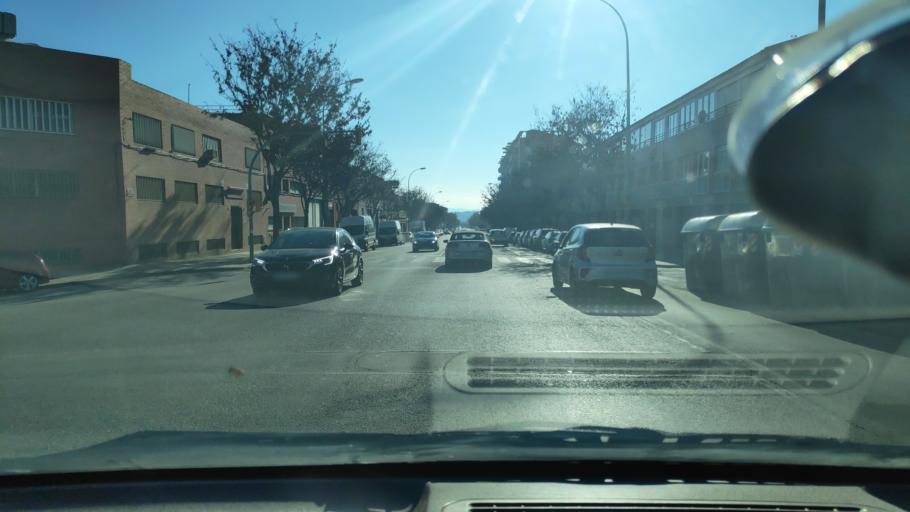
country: ES
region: Catalonia
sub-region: Provincia de Barcelona
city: Sabadell
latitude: 41.5485
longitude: 2.0948
